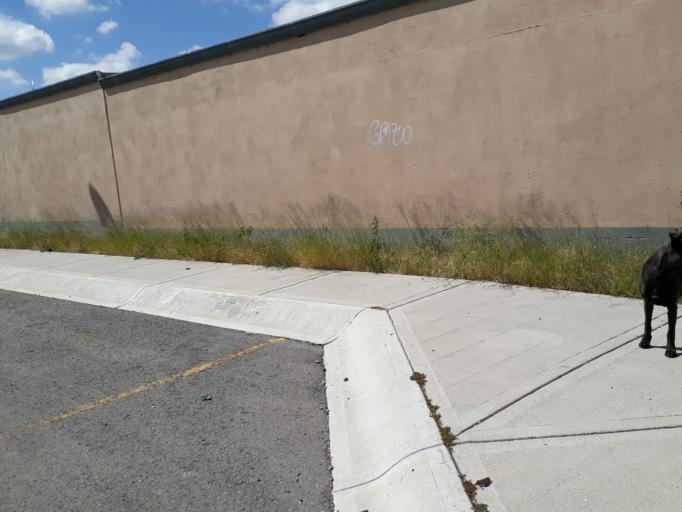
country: MX
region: Aguascalientes
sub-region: Aguascalientes
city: San Sebastian [Fraccionamiento]
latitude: 21.7949
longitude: -102.2732
